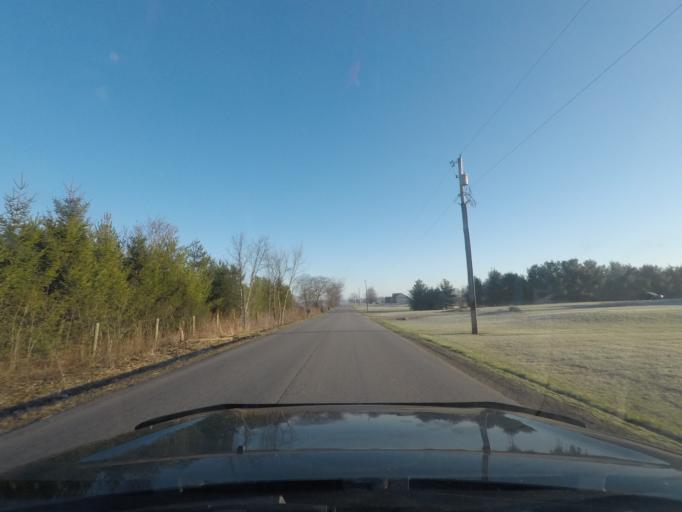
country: US
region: Indiana
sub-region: Elkhart County
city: Dunlap
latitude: 41.5557
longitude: -85.9249
